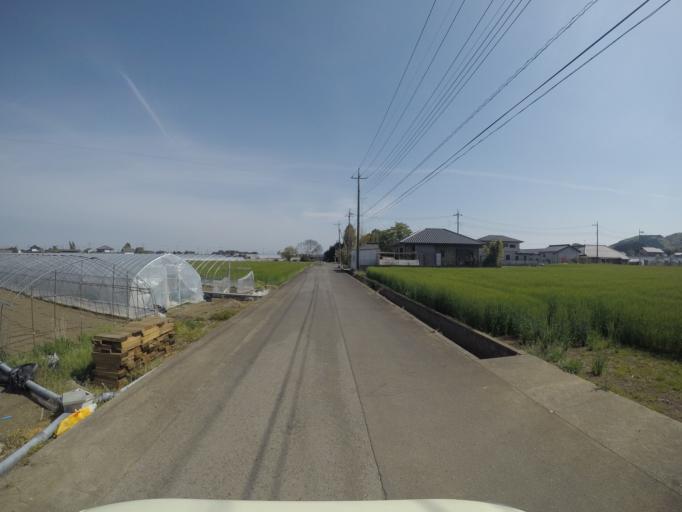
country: JP
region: Tochigi
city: Tochigi
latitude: 36.4450
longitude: 139.7209
